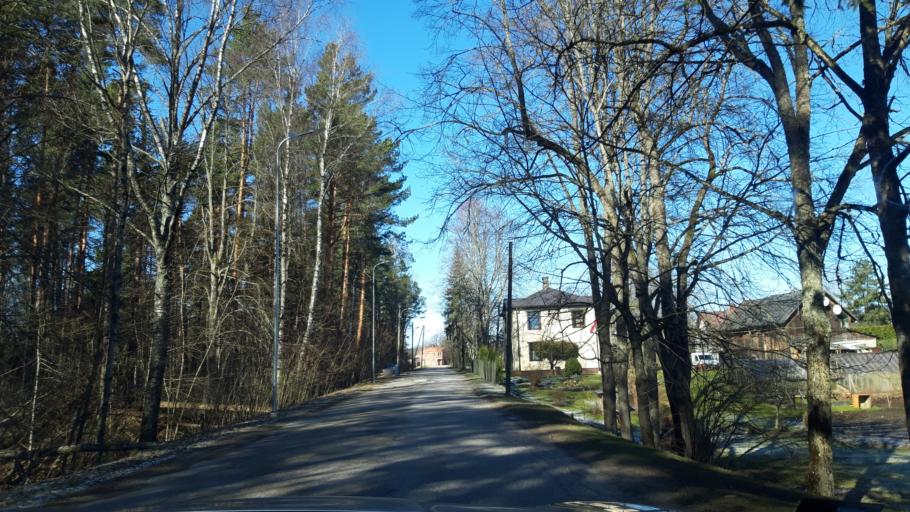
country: LV
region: Strenci
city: Strenci
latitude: 57.6220
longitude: 25.6976
